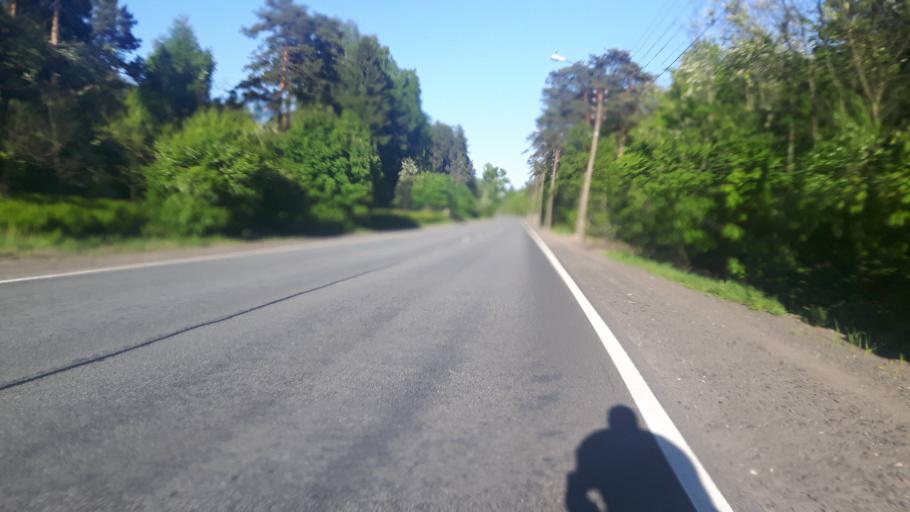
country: RU
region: Leningrad
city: Molodezhnoye
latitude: 60.1800
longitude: 29.4636
